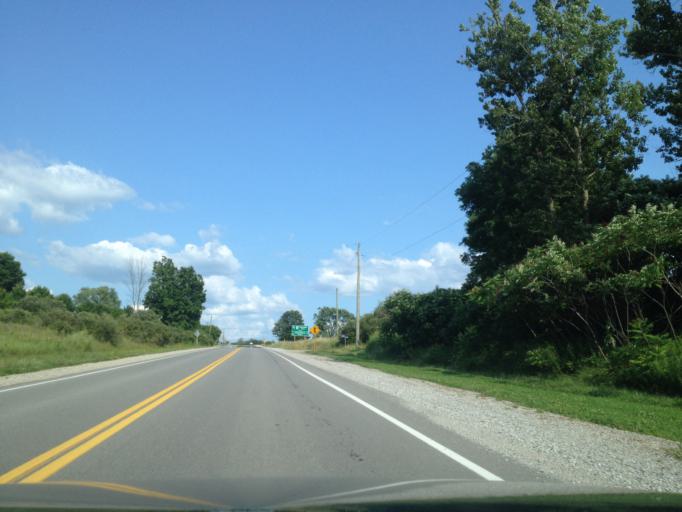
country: CA
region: Ontario
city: Aylmer
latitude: 42.7595
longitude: -80.8361
